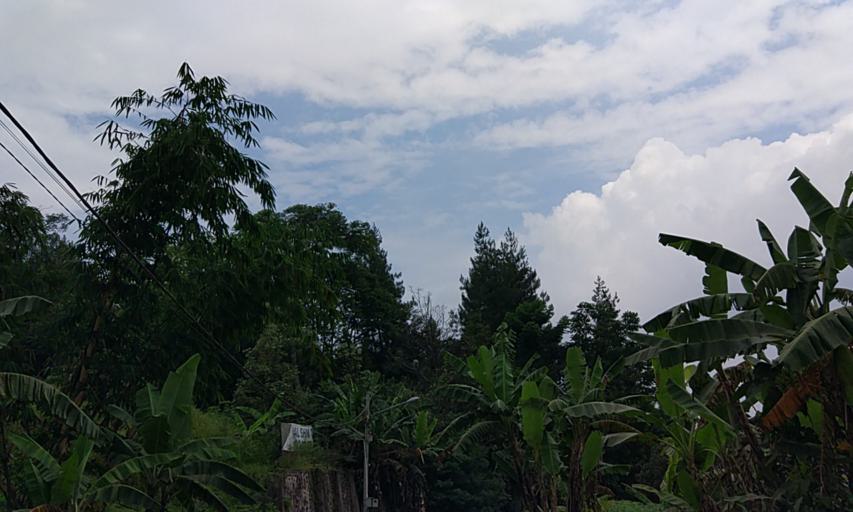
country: ID
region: West Java
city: Bandung
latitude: -6.8785
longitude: 107.6935
